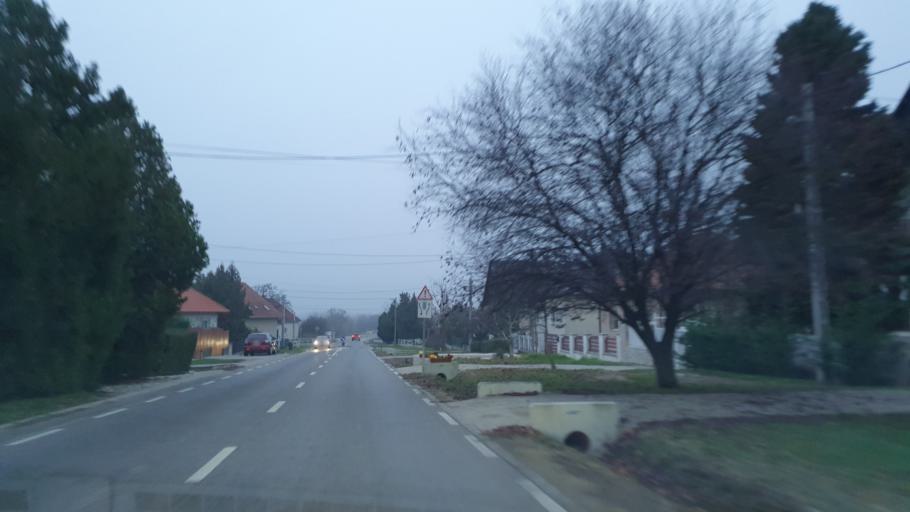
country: HU
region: Pest
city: Csomor
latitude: 47.5391
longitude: 19.2237
